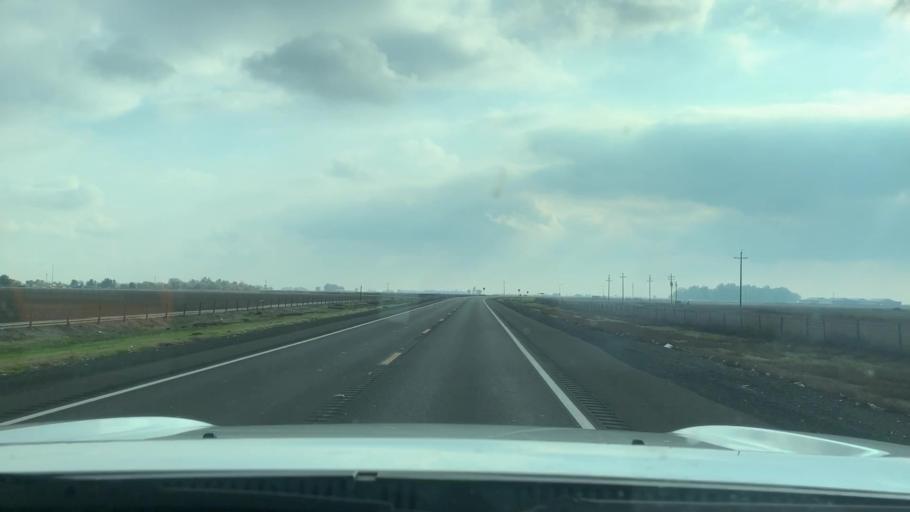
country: US
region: California
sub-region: Kings County
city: Lemoore
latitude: 36.2611
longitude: -119.8077
